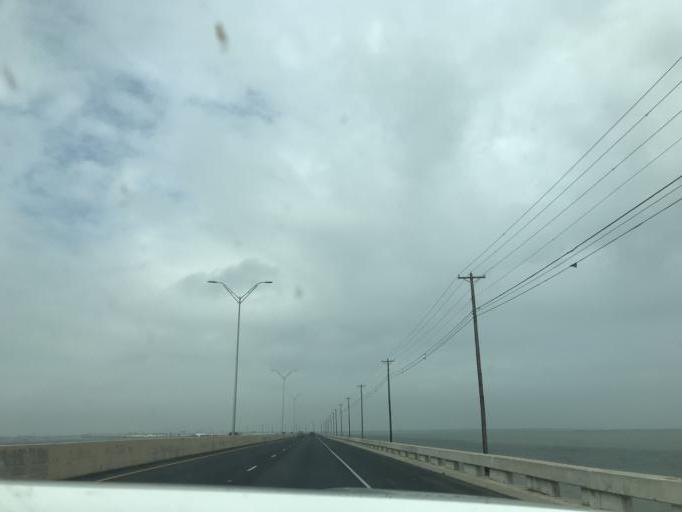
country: US
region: Texas
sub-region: Nueces County
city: Corpus Christi
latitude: 27.6498
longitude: -97.2533
